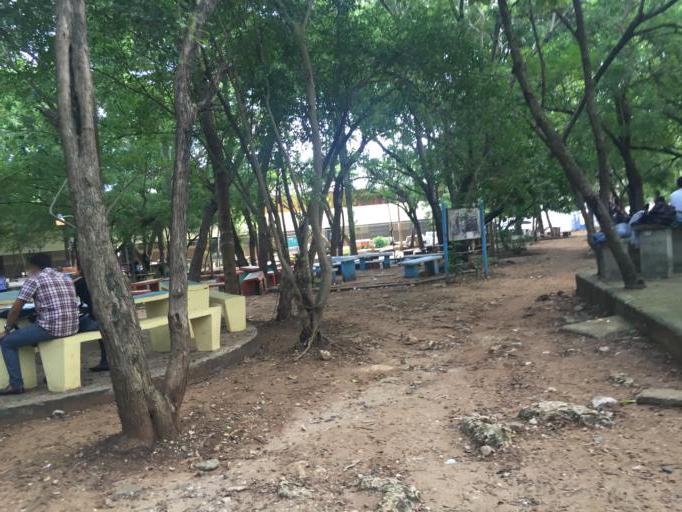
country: DO
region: Nacional
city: La Julia
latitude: 18.4607
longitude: -69.9172
